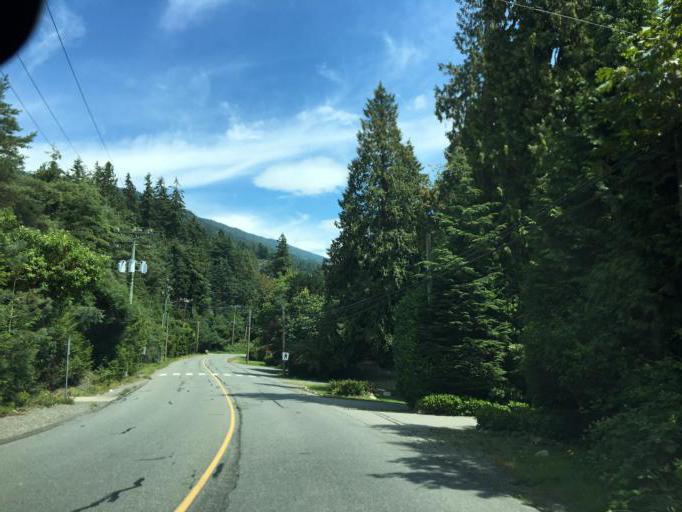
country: CA
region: British Columbia
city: West Vancouver
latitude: 49.3407
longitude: -123.2360
